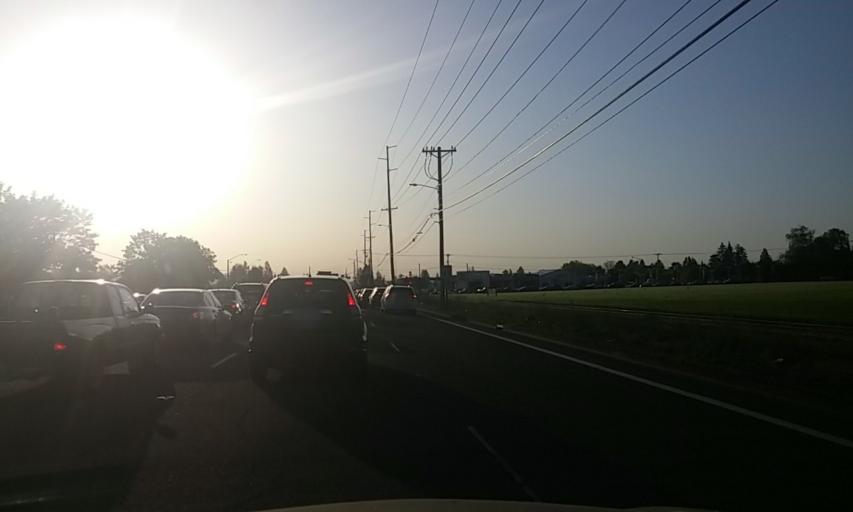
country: US
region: Oregon
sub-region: Washington County
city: Beaverton
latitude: 45.4898
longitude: -122.8289
